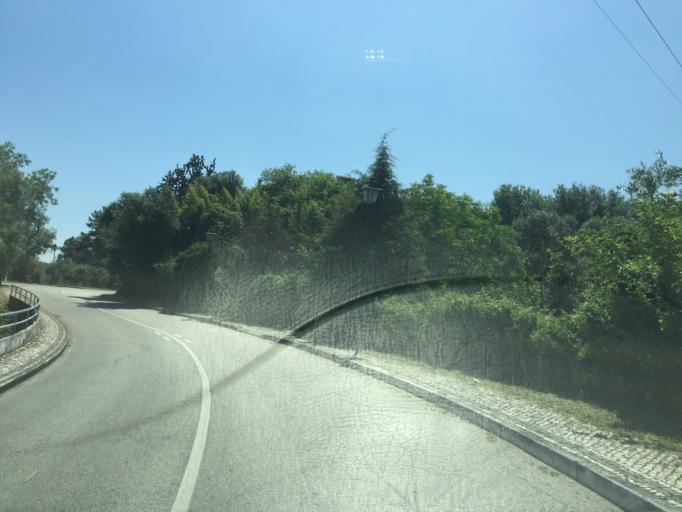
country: PT
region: Santarem
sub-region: Constancia
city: Constancia
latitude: 39.4800
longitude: -8.3341
